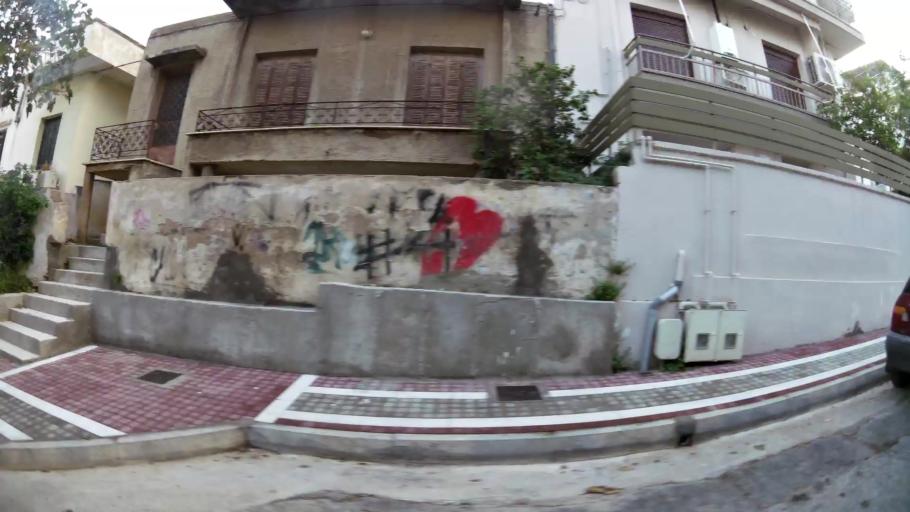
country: GR
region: Attica
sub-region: Nomarchia Athinas
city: Ymittos
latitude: 37.9503
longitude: 23.7470
